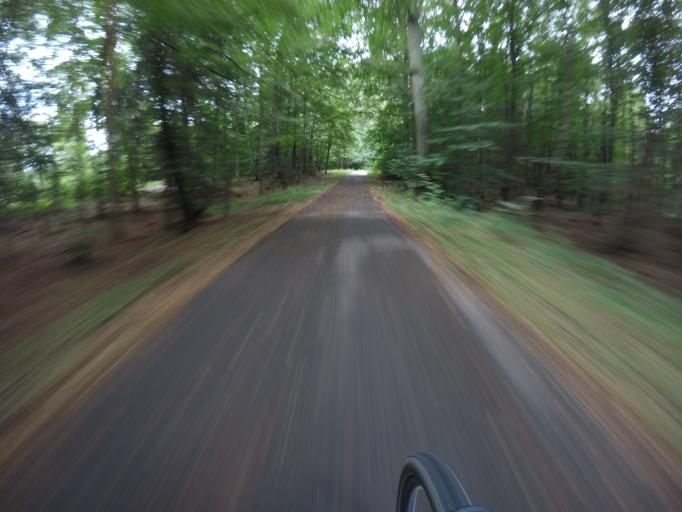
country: DE
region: Baden-Wuerttemberg
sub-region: Regierungsbezirk Stuttgart
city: Sindelfingen
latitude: 48.7249
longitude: 9.0621
